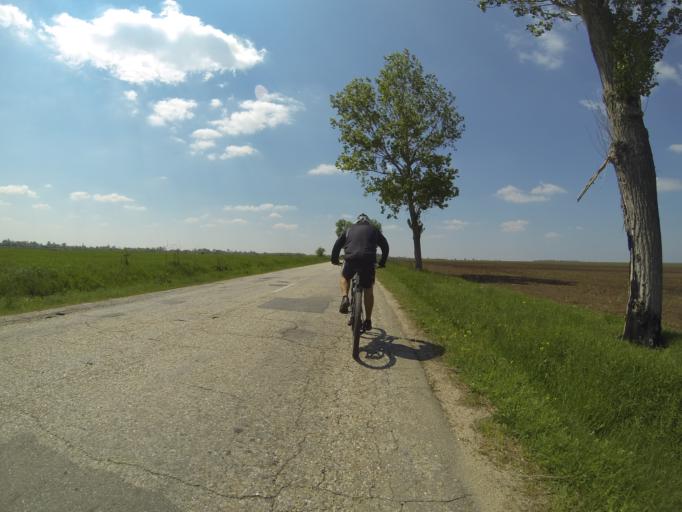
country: RO
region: Dolj
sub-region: Comuna Salcuta
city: Salcuta
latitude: 44.2560
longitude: 23.4365
